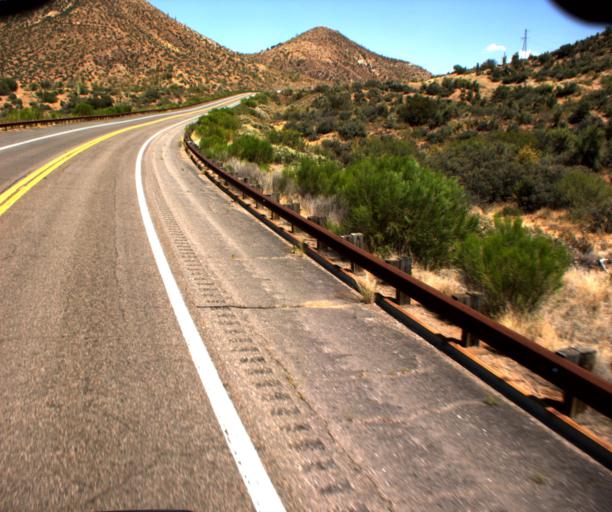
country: US
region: Arizona
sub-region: Gila County
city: Claypool
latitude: 33.5262
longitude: -110.8994
